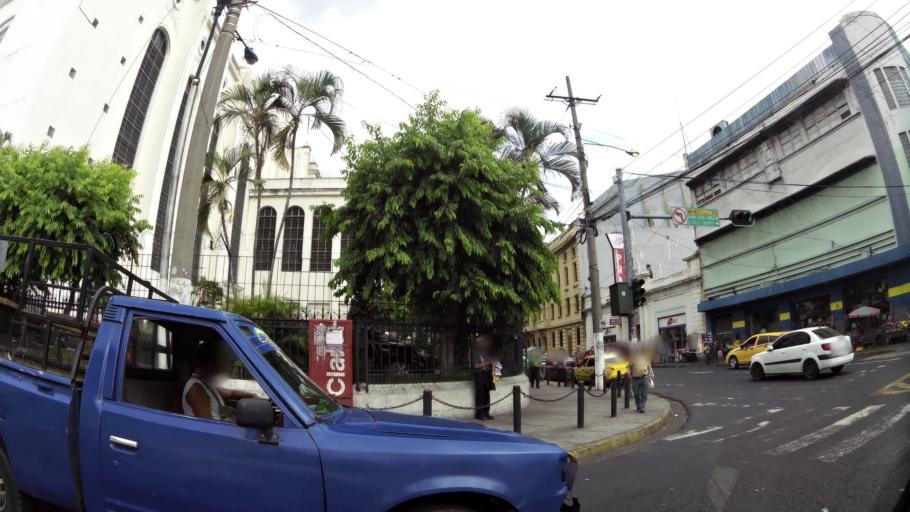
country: SV
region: San Salvador
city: San Salvador
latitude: 13.6980
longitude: -89.1908
